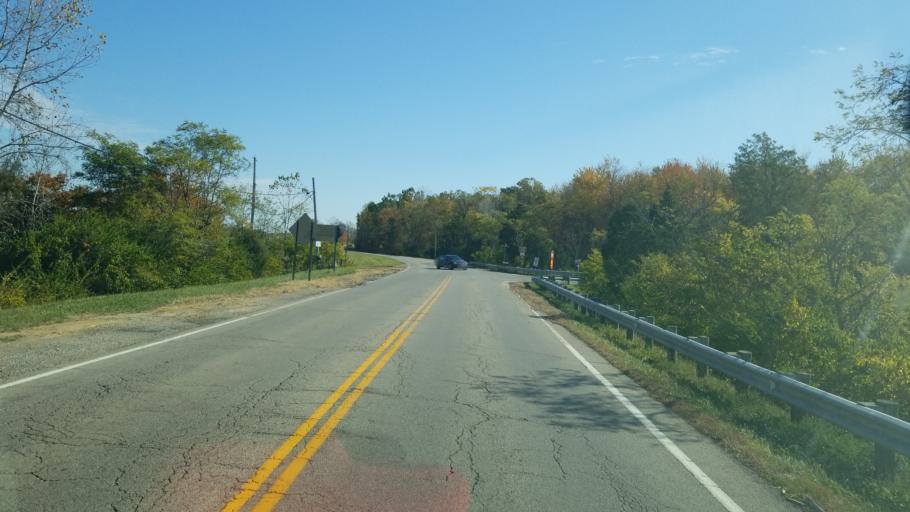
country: US
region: Ohio
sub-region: Warren County
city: Morrow
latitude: 39.4296
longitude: -84.0774
